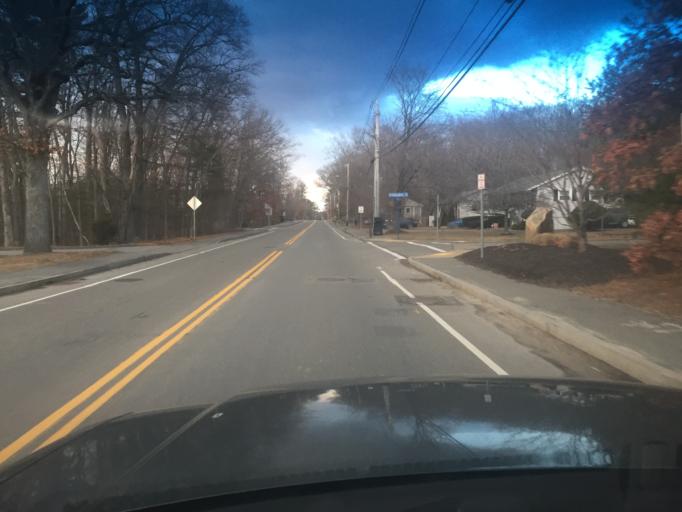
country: US
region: Massachusetts
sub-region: Norfolk County
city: Medway
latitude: 42.1453
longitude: -71.4429
